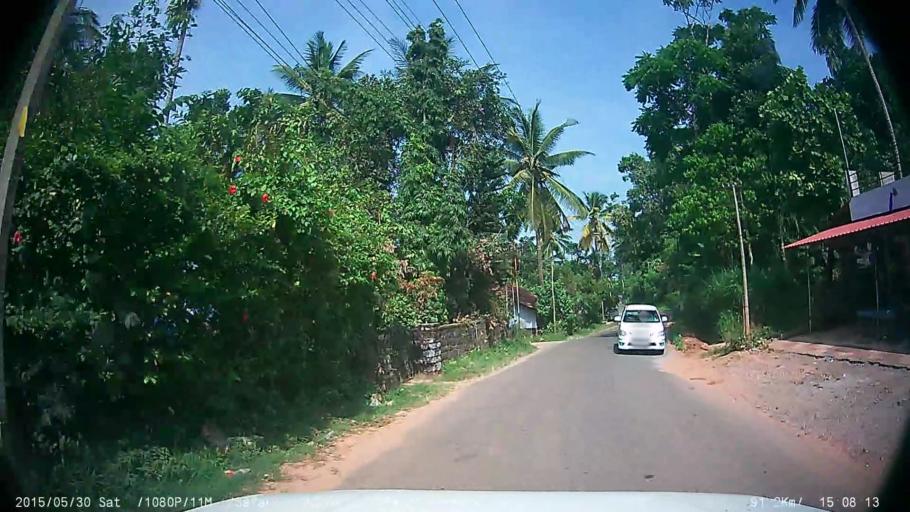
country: IN
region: Kerala
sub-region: Wayanad
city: Panamaram
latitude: 11.8002
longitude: 76.0194
